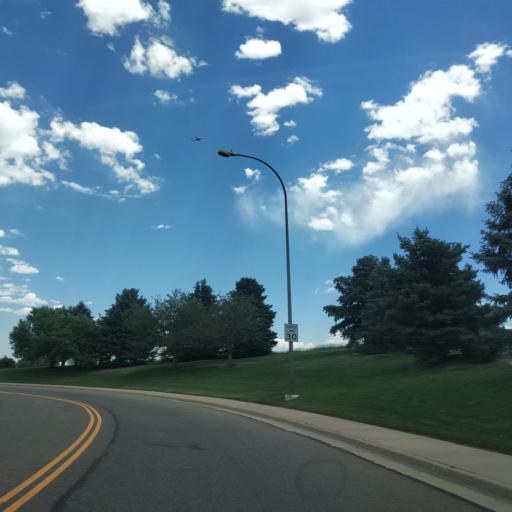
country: US
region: Colorado
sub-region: Jefferson County
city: Lakewood
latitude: 39.7038
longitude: -105.1091
